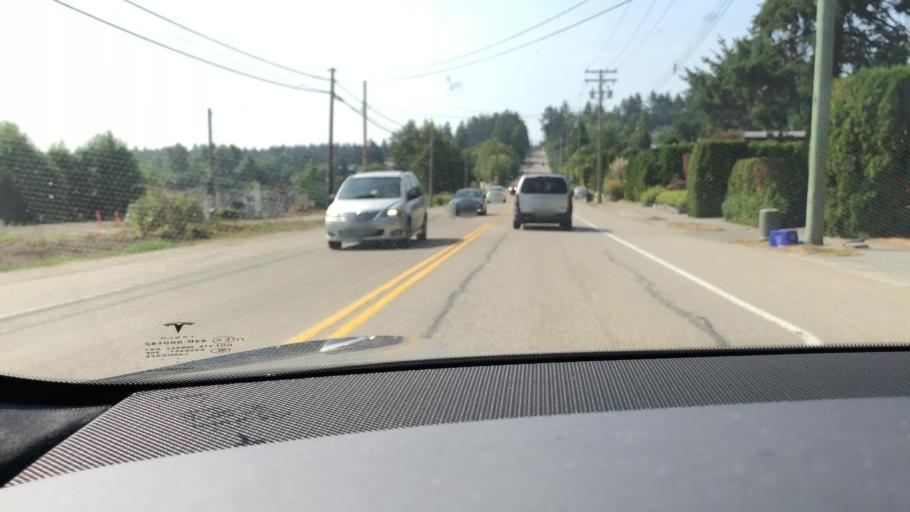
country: US
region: Washington
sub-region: Whatcom County
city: Point Roberts
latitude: 49.0123
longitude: -123.0687
